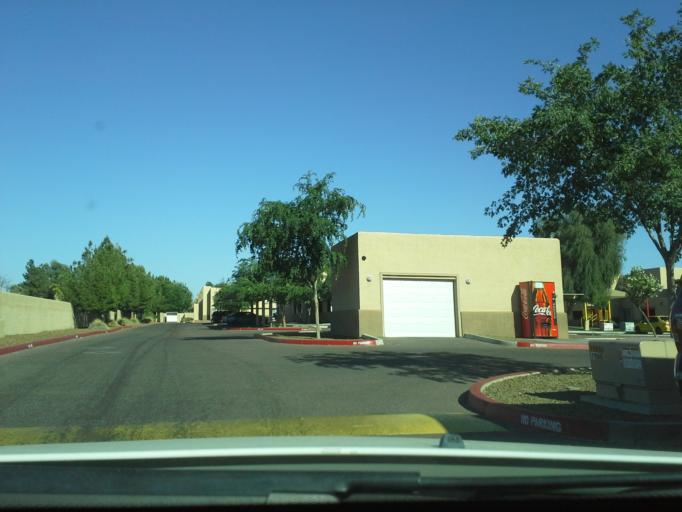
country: US
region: Arizona
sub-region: Maricopa County
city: Glendale
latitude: 33.5371
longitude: -112.2103
